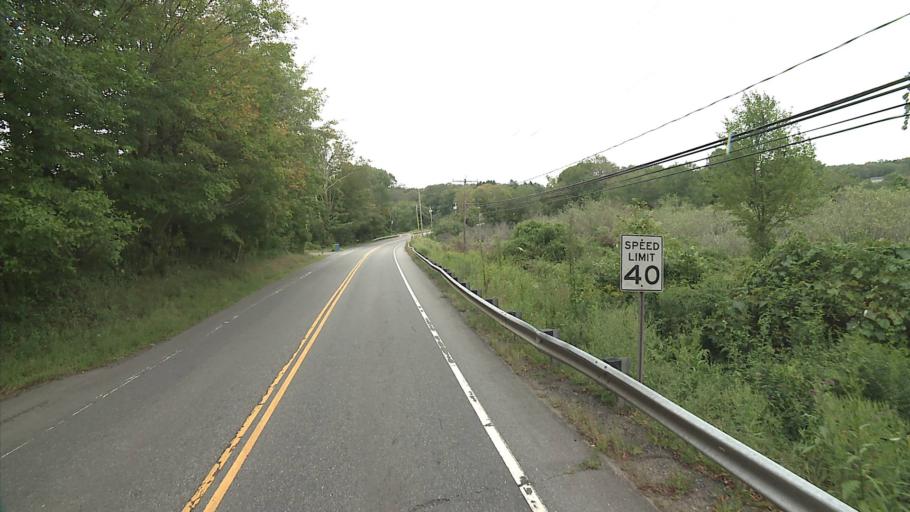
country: US
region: Connecticut
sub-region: Tolland County
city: Hebron
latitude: 41.6360
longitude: -72.3450
